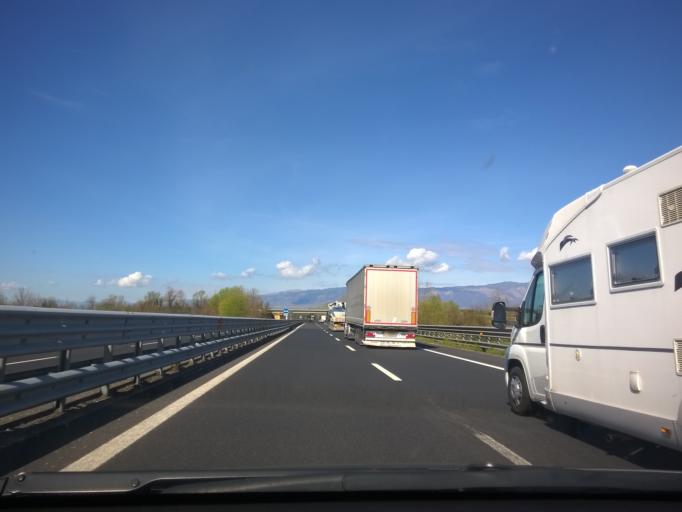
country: IT
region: Friuli Venezia Giulia
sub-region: Provincia di Pordenone
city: Azzano Decimo
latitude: 45.9298
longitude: 12.6774
